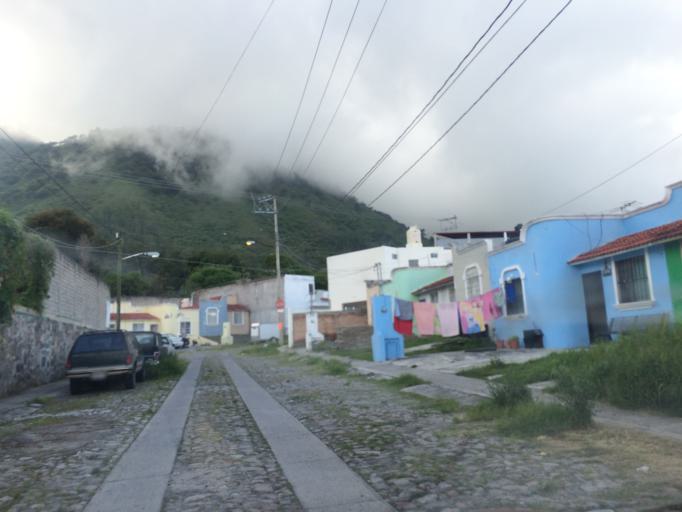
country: MX
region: Nayarit
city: Tepic
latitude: 21.4975
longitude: -104.9190
